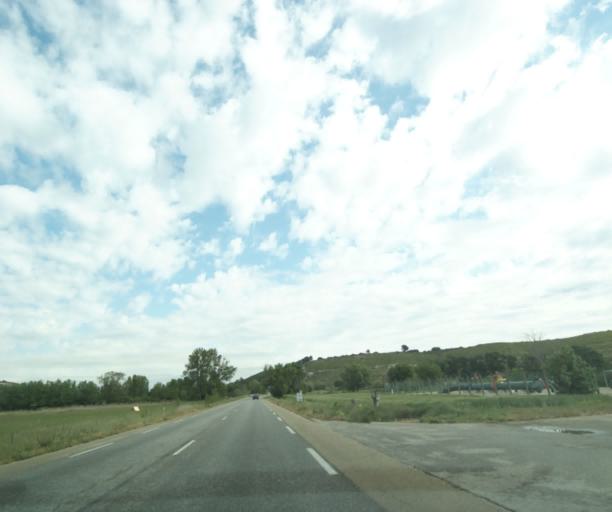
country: FR
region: Provence-Alpes-Cote d'Azur
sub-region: Departement des Bouches-du-Rhone
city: Cabries
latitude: 43.4755
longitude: 5.3555
